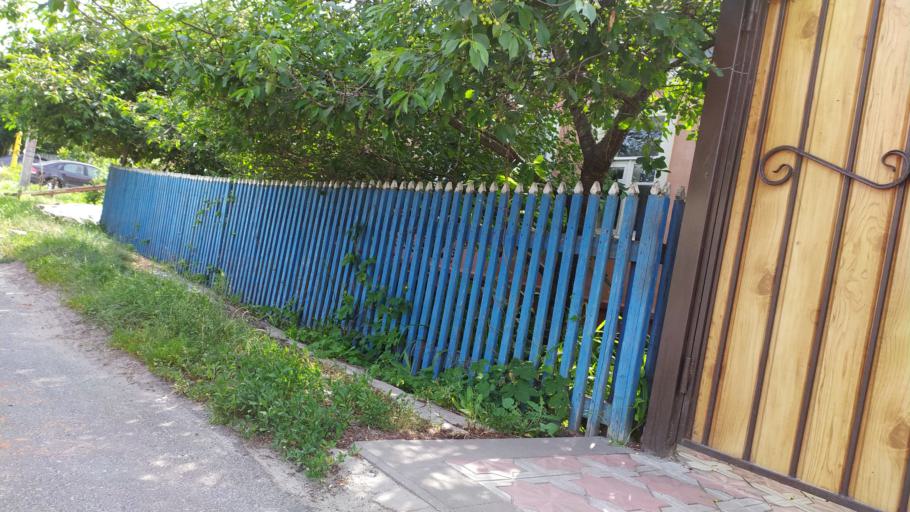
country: RU
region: Kursk
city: Kursk
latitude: 51.6617
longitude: 36.1538
